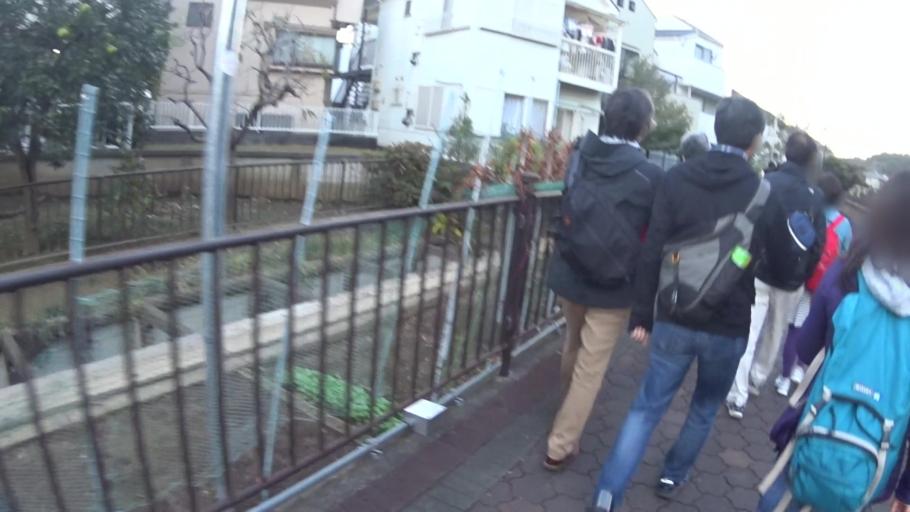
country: JP
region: Tokyo
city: Chofugaoka
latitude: 35.6328
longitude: 139.5252
